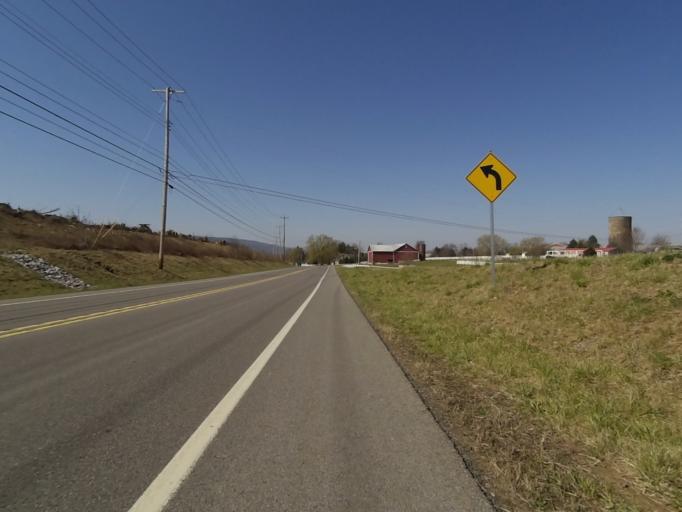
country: US
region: Pennsylvania
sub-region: Centre County
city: Pine Grove Mills
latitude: 40.7330
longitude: -77.9267
